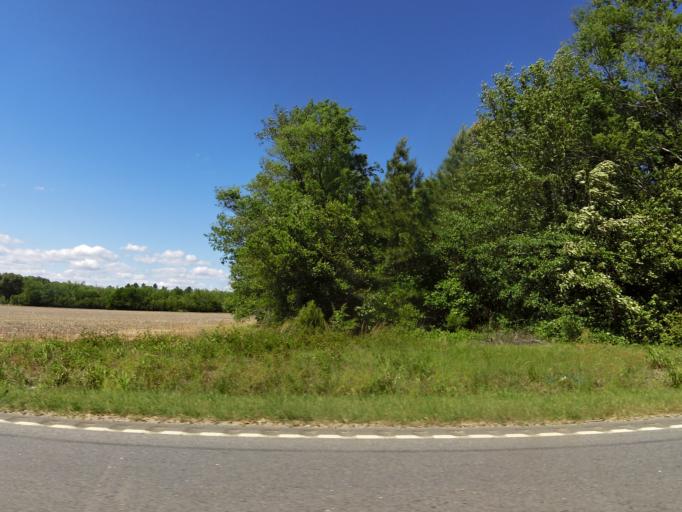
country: US
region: South Carolina
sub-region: Aiken County
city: Aiken
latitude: 33.5379
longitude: -81.6547
